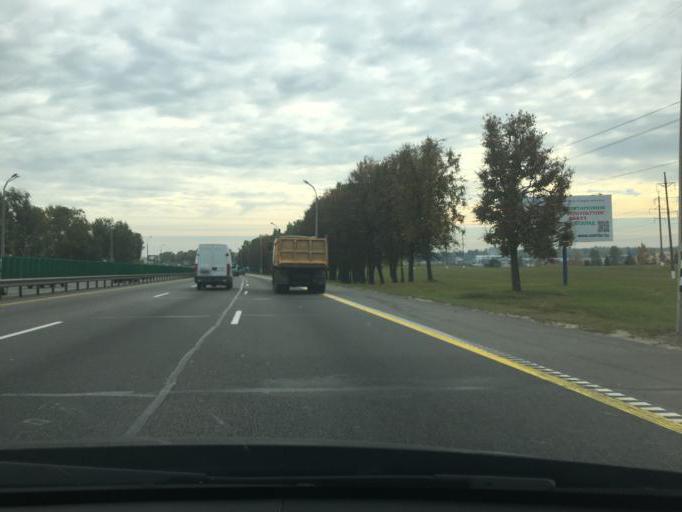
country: BY
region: Minsk
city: Malinovka
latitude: 53.8586
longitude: 27.4281
